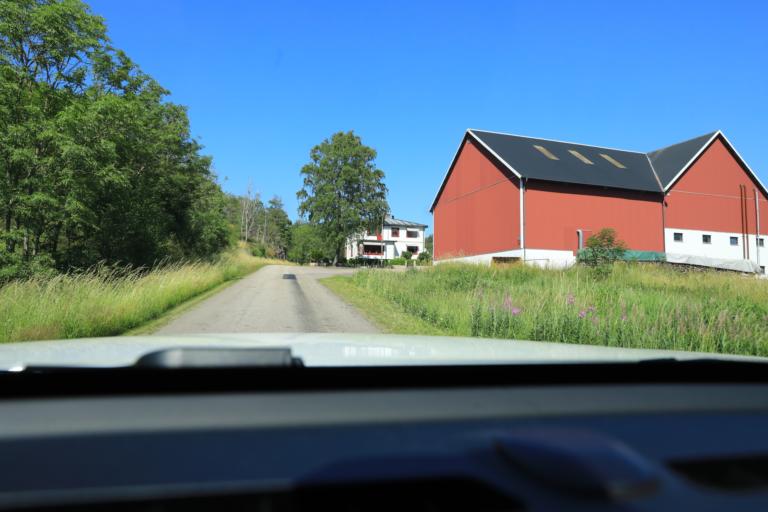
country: SE
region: Halland
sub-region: Varbergs Kommun
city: Veddige
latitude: 57.1877
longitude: 12.3183
